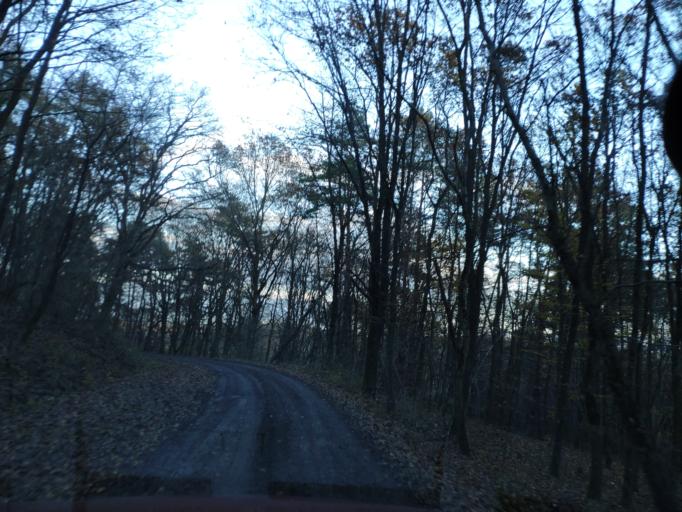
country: SK
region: Kosicky
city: Secovce
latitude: 48.6039
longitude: 21.5177
